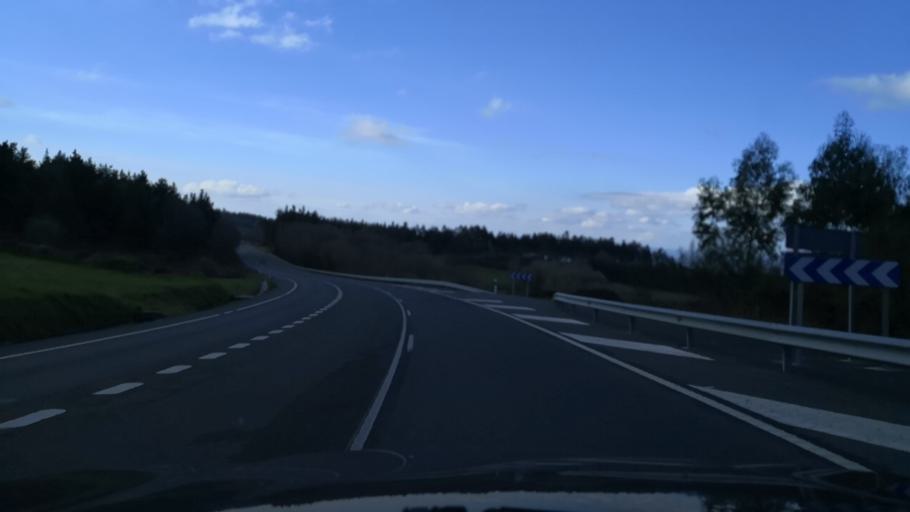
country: ES
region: Galicia
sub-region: Provincia de Pontevedra
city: Silleda
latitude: 42.7086
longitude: -8.3479
